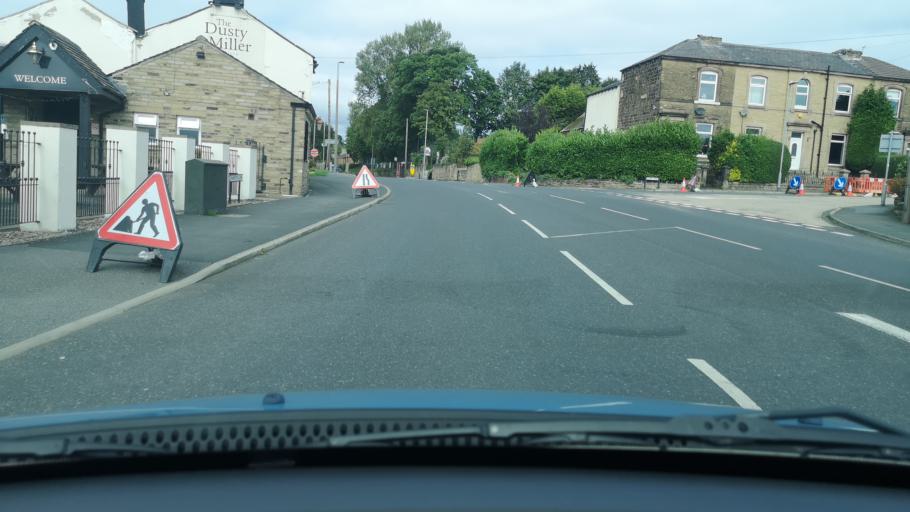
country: GB
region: England
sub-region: Kirklees
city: Mirfield
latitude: 53.6820
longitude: -1.6852
